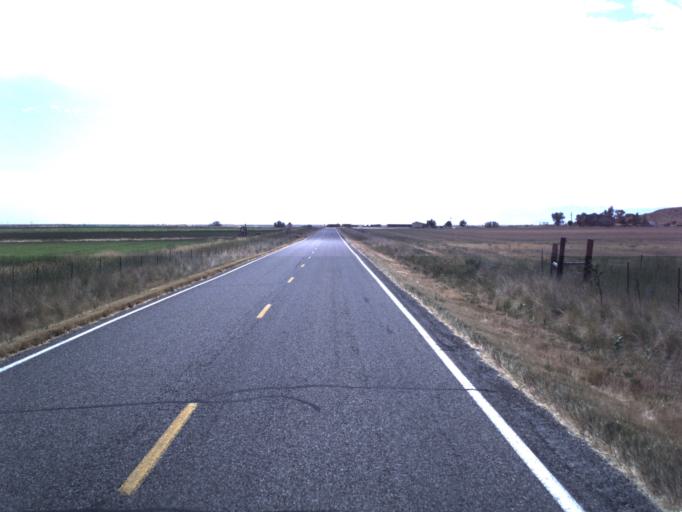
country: US
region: Utah
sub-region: Box Elder County
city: Tremonton
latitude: 41.6339
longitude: -112.3309
